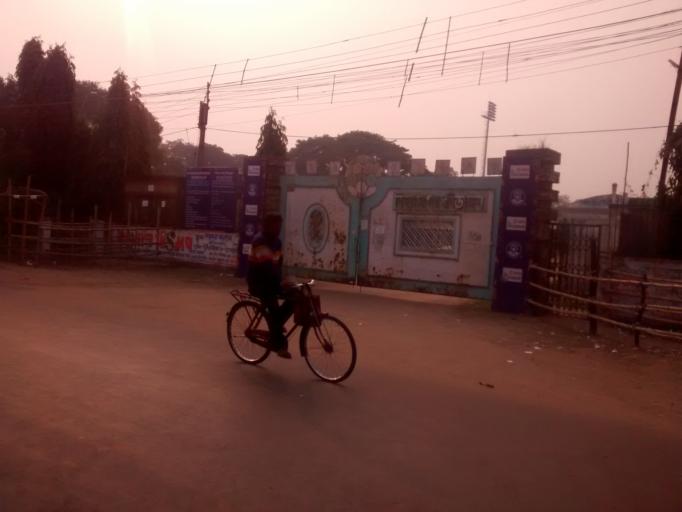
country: IN
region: West Bengal
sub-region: North 24 Parganas
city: Barasat
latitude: 22.7172
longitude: 88.4802
